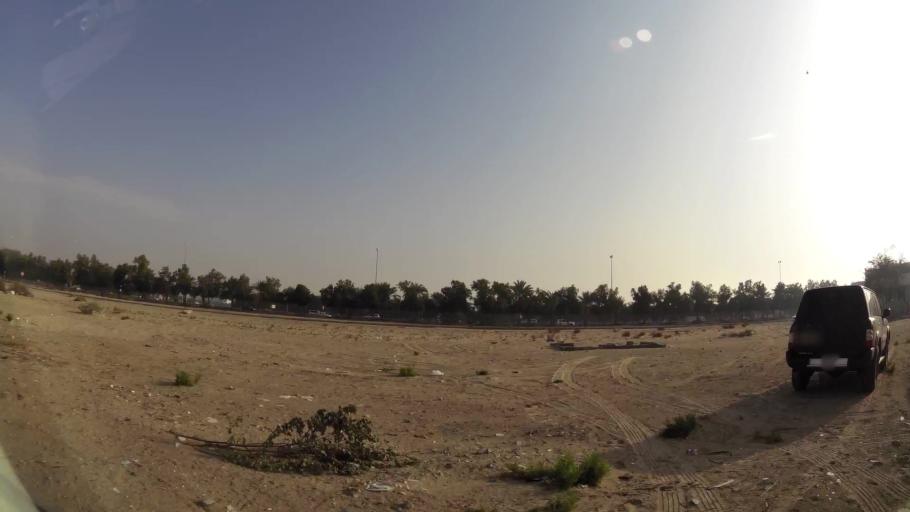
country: AE
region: Abu Dhabi
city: Abu Dhabi
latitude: 24.2984
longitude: 54.6245
